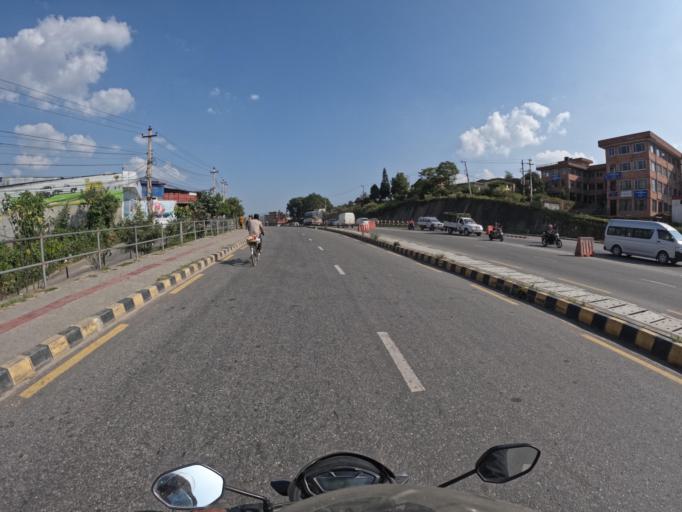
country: NP
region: Central Region
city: Kirtipur
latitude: 27.6858
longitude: 85.2933
